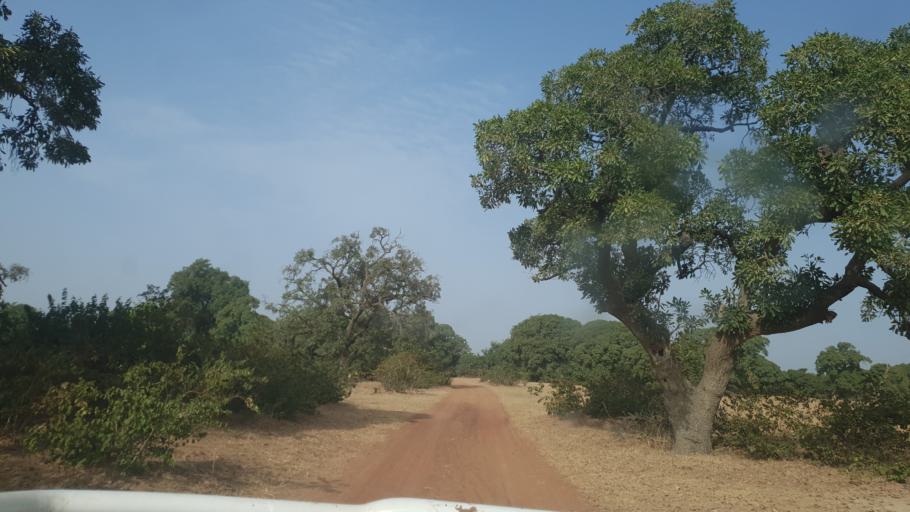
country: ML
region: Segou
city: Baroueli
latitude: 13.3591
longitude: -6.9233
